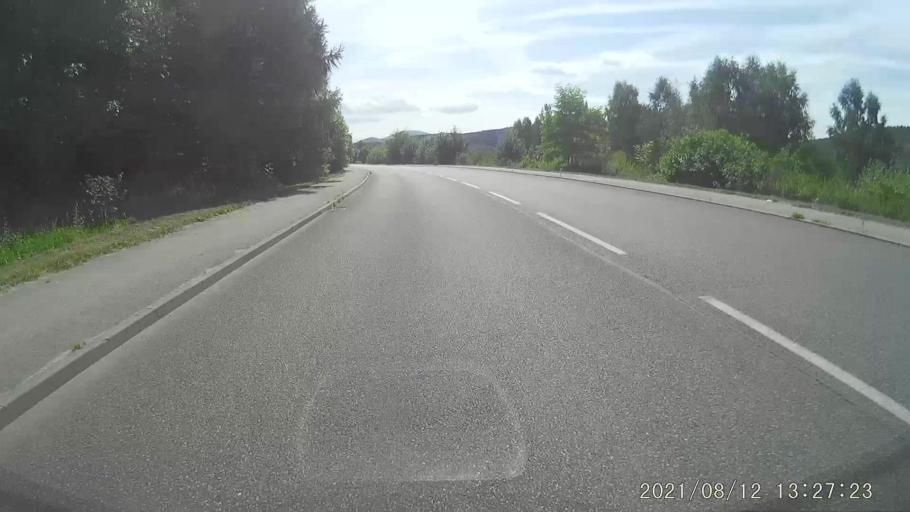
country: PL
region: Lower Silesian Voivodeship
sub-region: Powiat klodzki
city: Ladek-Zdroj
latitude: 50.3338
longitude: 16.8690
